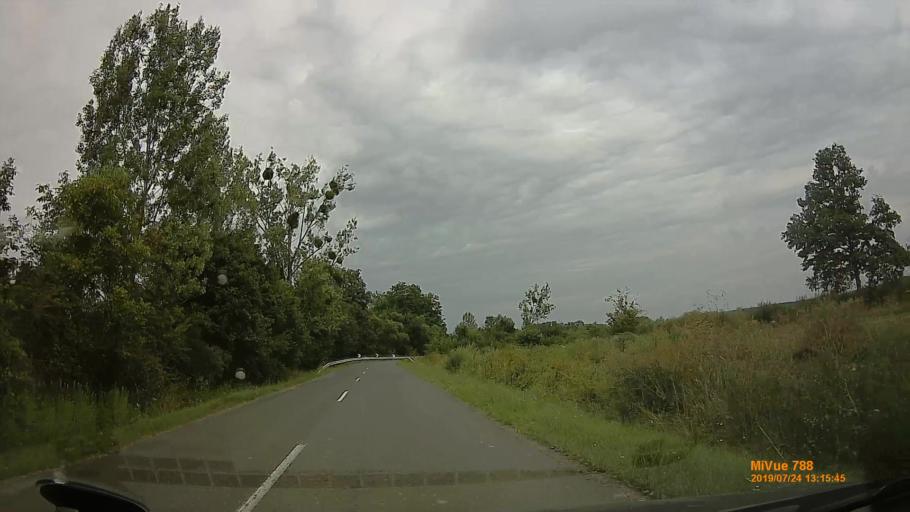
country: HU
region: Szabolcs-Szatmar-Bereg
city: Vasarosnameny
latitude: 48.1922
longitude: 22.3606
